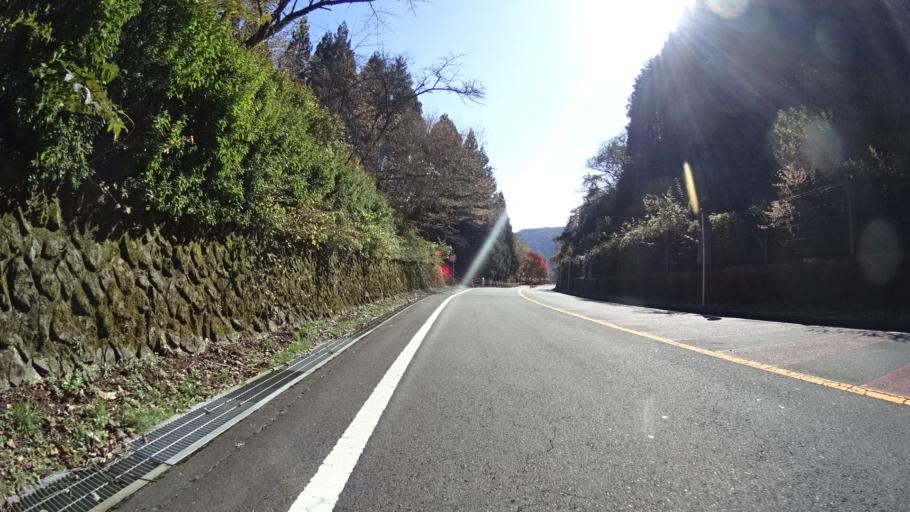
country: JP
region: Yamanashi
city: Uenohara
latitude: 35.7398
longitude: 139.0383
